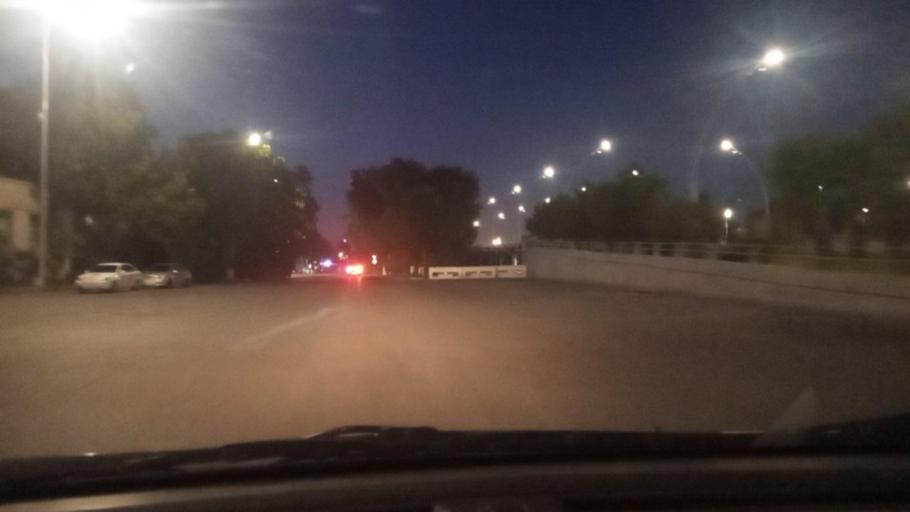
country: UZ
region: Toshkent Shahri
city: Tashkent
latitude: 41.2706
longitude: 69.2607
